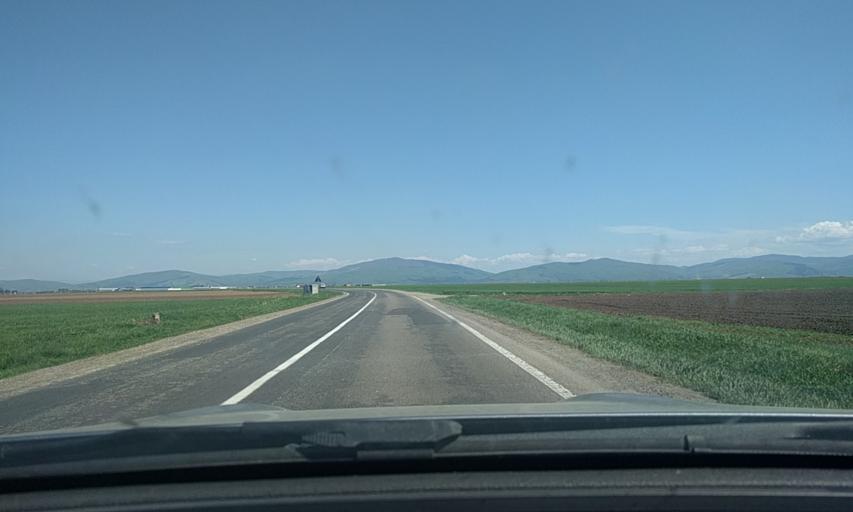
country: RO
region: Brasov
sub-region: Comuna Harman
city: Harman
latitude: 45.7103
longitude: 25.7101
